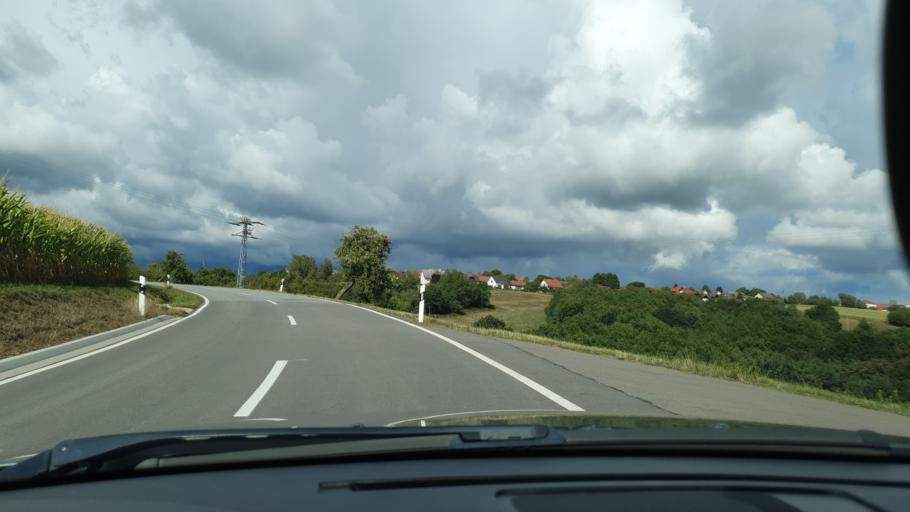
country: DE
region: Rheinland-Pfalz
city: Wallhalben
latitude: 49.3184
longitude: 7.5407
